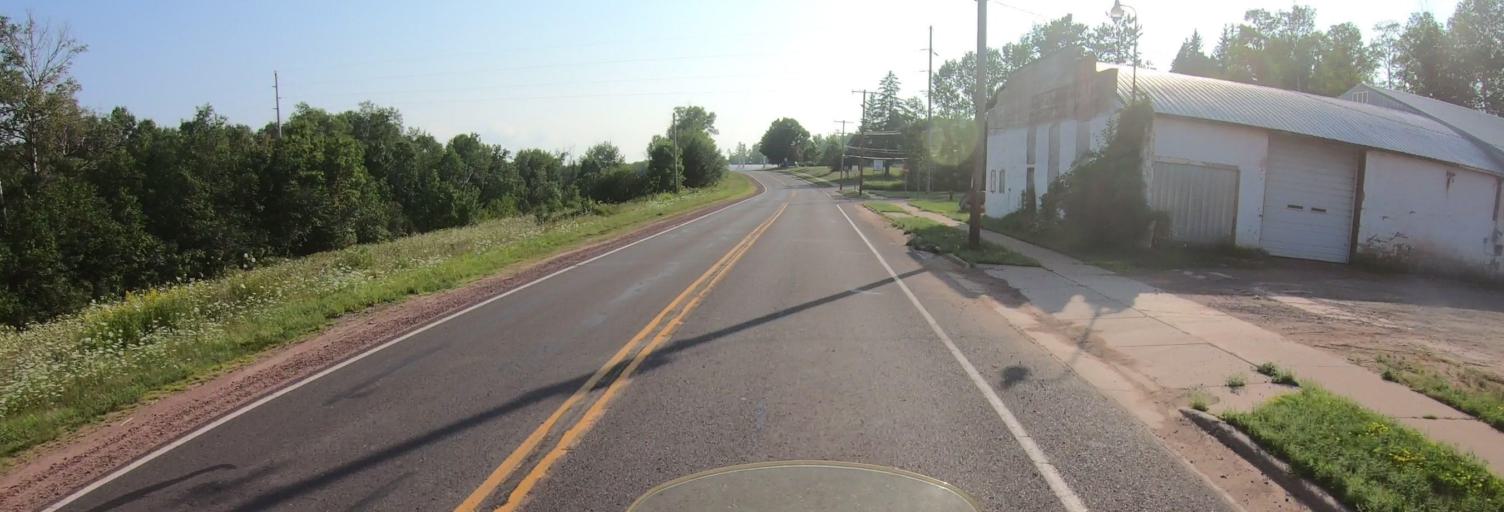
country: US
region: Wisconsin
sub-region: Ashland County
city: Ashland
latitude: 46.3233
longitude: -90.6656
